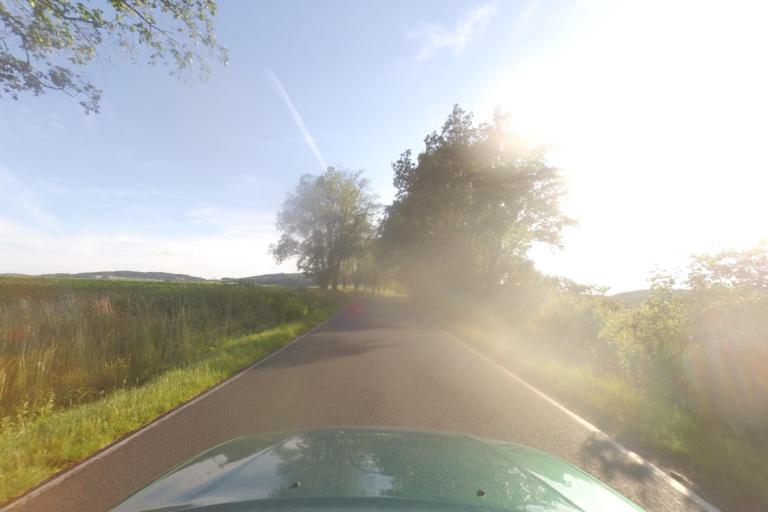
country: PL
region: Lower Silesian Voivodeship
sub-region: Powiat dzierzoniowski
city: Niemcza
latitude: 50.7187
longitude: 16.8136
